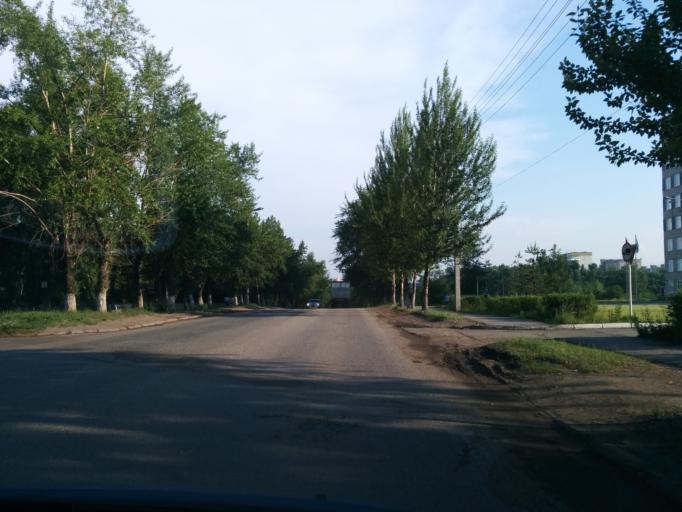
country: RU
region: Perm
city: Perm
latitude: 58.1203
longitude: 56.2928
